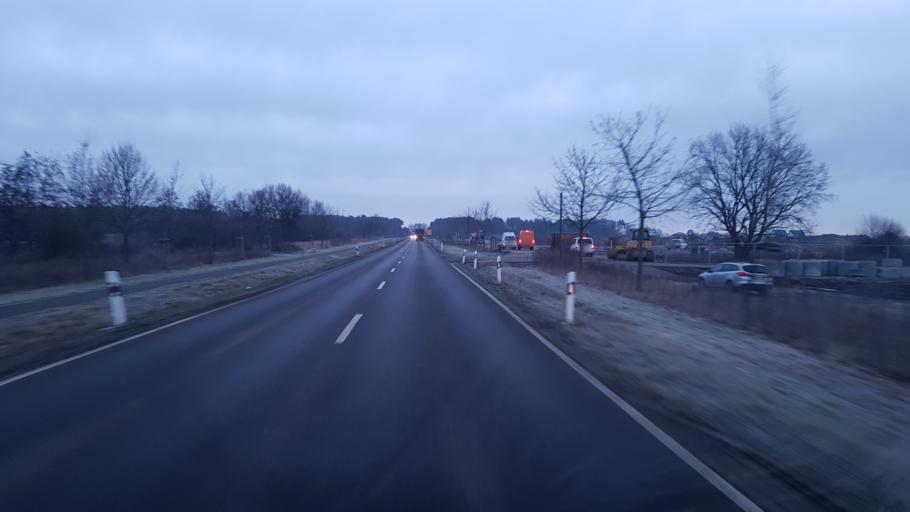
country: DE
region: Brandenburg
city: Ludwigsfelde
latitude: 52.3109
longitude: 13.2076
